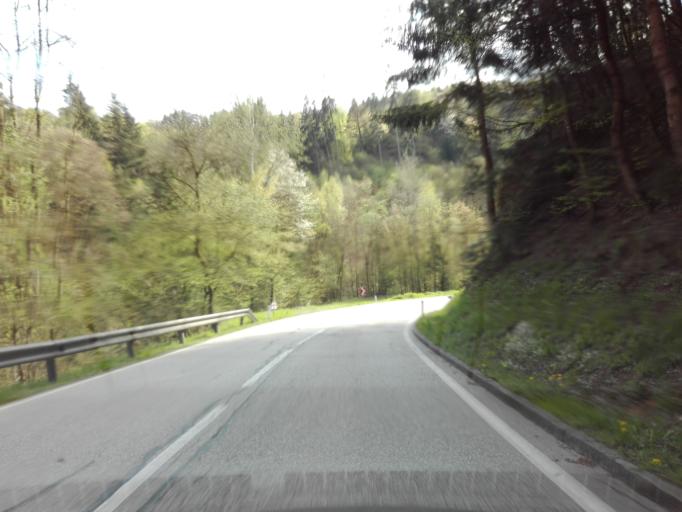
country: AT
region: Upper Austria
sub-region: Politischer Bezirk Urfahr-Umgebung
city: Feldkirchen an der Donau
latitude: 48.3835
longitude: 14.0784
